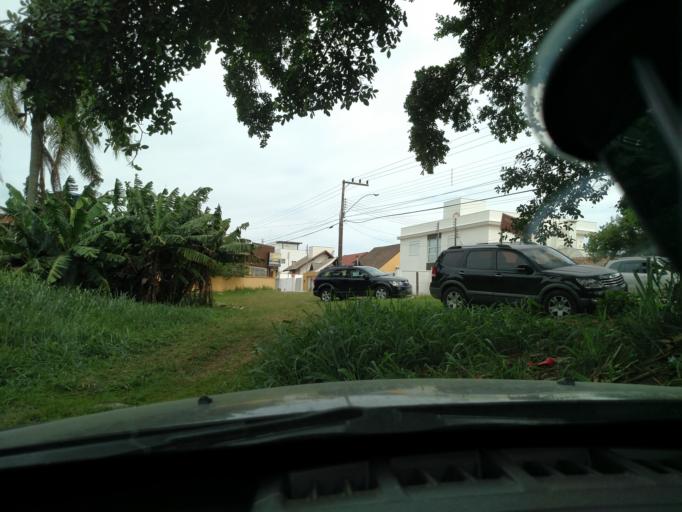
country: BR
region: Santa Catarina
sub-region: Porto Belo
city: Porto Belo
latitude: -27.1871
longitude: -48.5097
